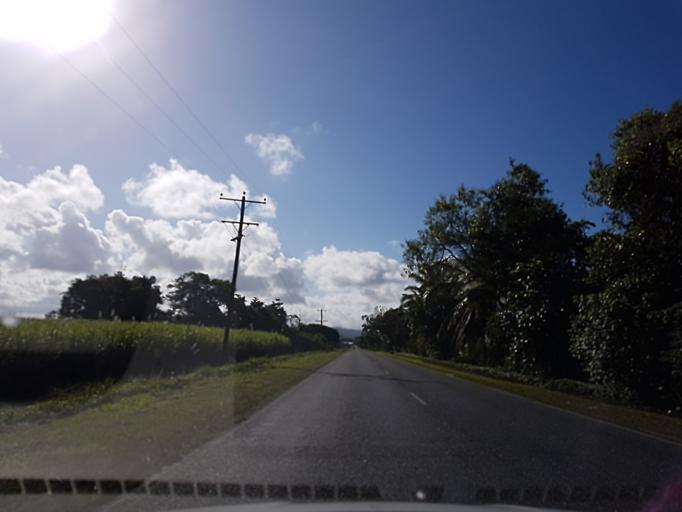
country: AU
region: Queensland
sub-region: Cairns
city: Port Douglas
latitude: -16.4141
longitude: 145.3847
